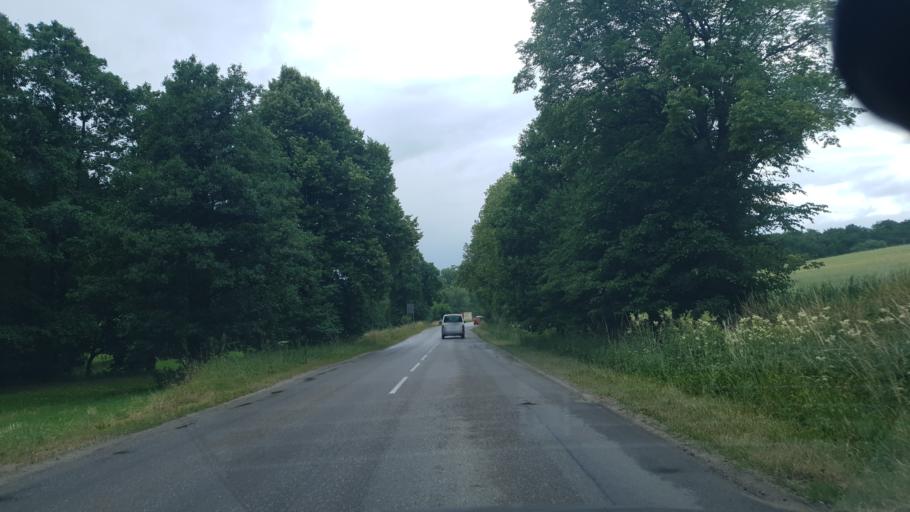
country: PL
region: Pomeranian Voivodeship
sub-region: Powiat kartuski
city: Przodkowo
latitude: 54.3599
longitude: 18.2586
